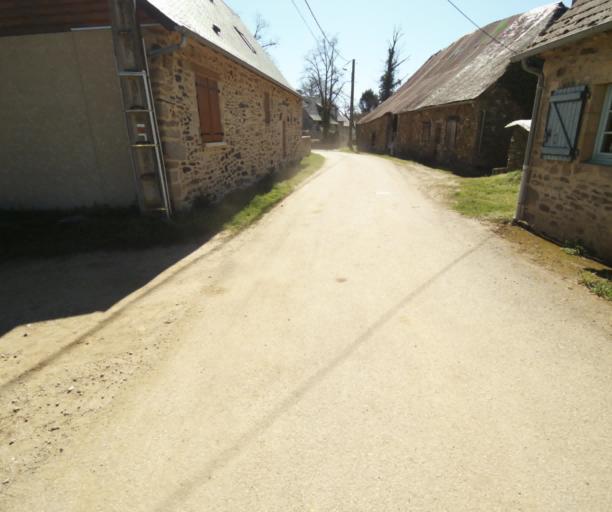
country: FR
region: Limousin
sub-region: Departement de la Correze
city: Chamboulive
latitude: 45.4274
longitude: 1.7216
